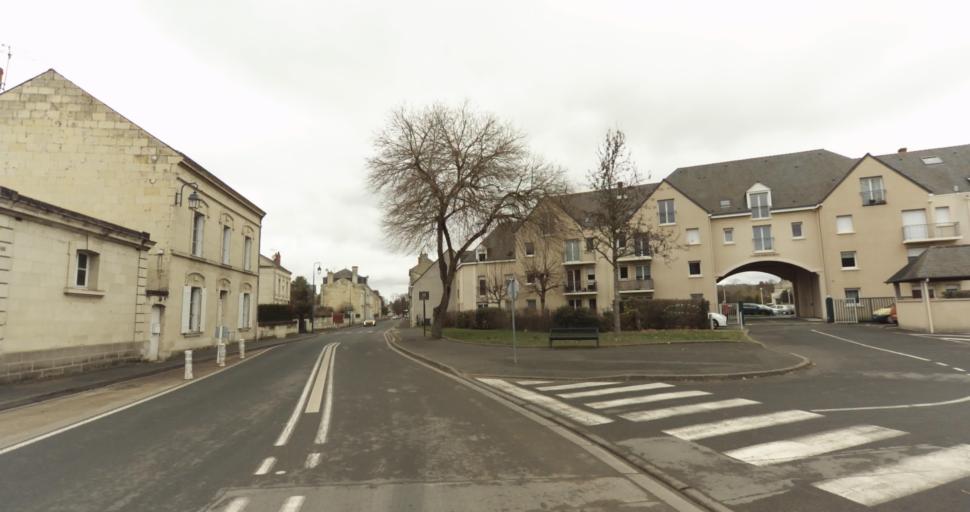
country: FR
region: Pays de la Loire
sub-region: Departement de Maine-et-Loire
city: Saumur
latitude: 47.2625
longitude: -0.0994
